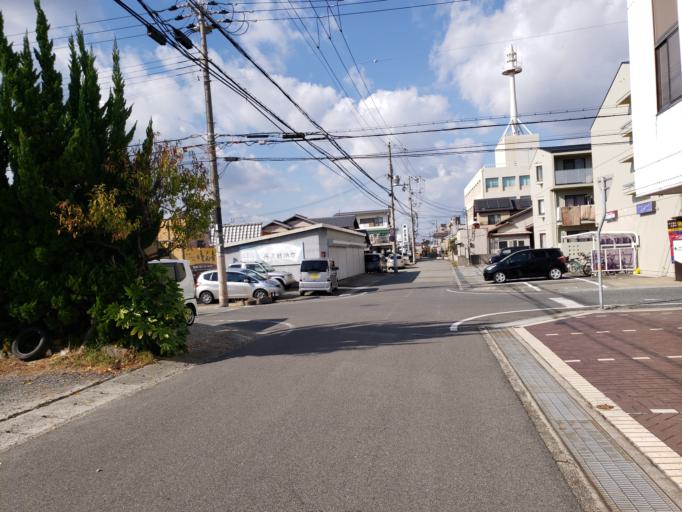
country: JP
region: Hyogo
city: Kakogawacho-honmachi
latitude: 34.7578
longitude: 134.8384
